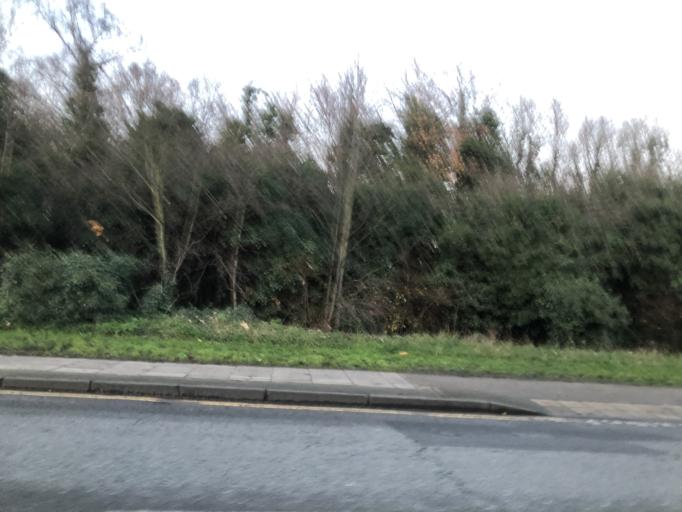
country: GB
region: England
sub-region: Greater London
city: Woolwich
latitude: 51.4723
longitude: 0.0487
